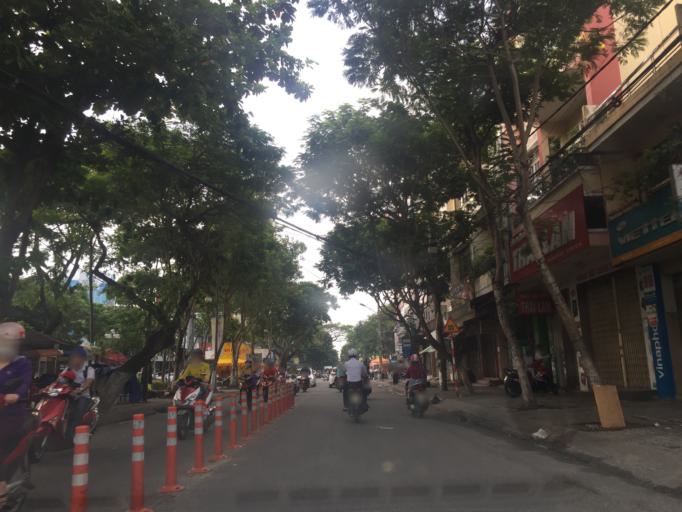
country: VN
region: Da Nang
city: Da Nang
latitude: 16.0733
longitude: 108.2129
